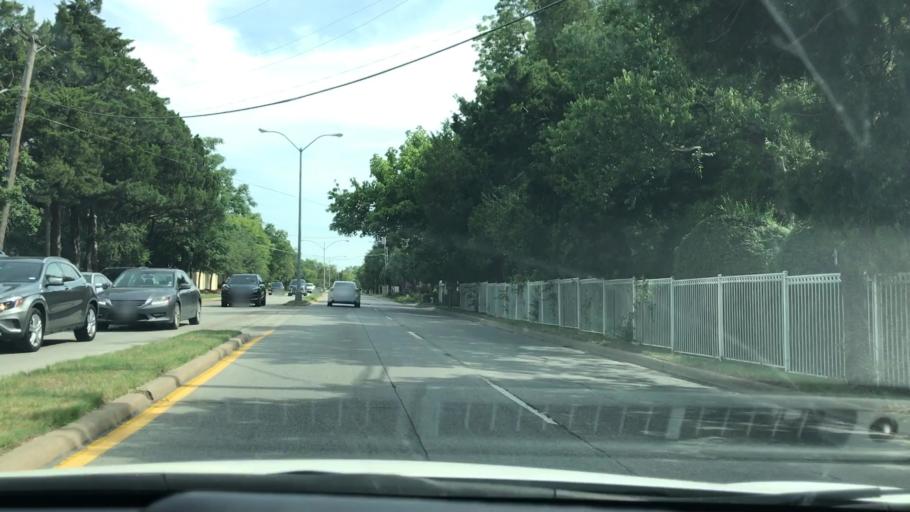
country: US
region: Texas
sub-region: Dallas County
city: University Park
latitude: 32.8733
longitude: -96.8213
